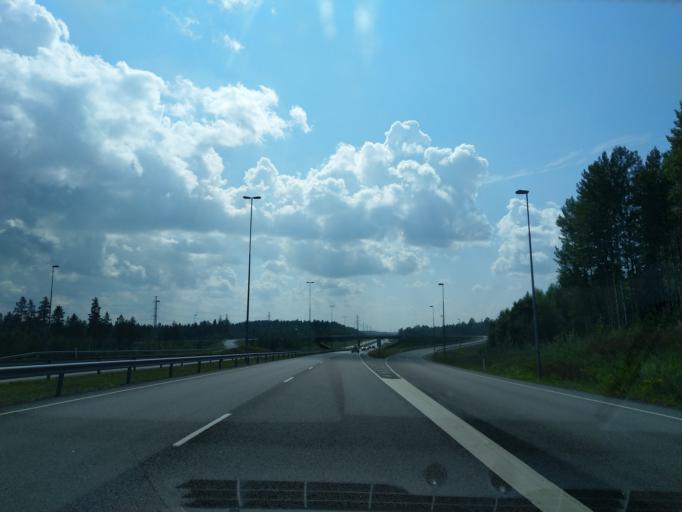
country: FI
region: South Karelia
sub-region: Lappeenranta
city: Joutseno
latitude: 61.0866
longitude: 28.3533
